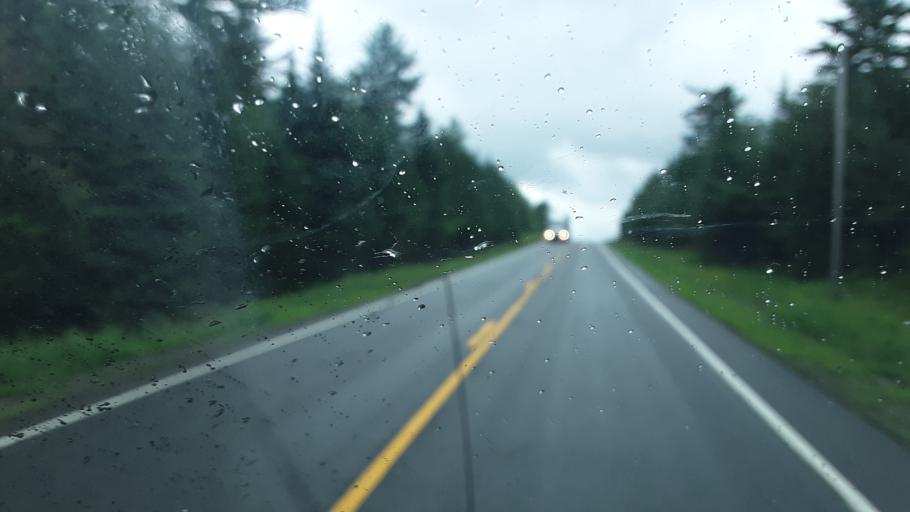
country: US
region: Maine
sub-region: Penobscot County
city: Patten
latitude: 46.4148
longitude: -68.3722
